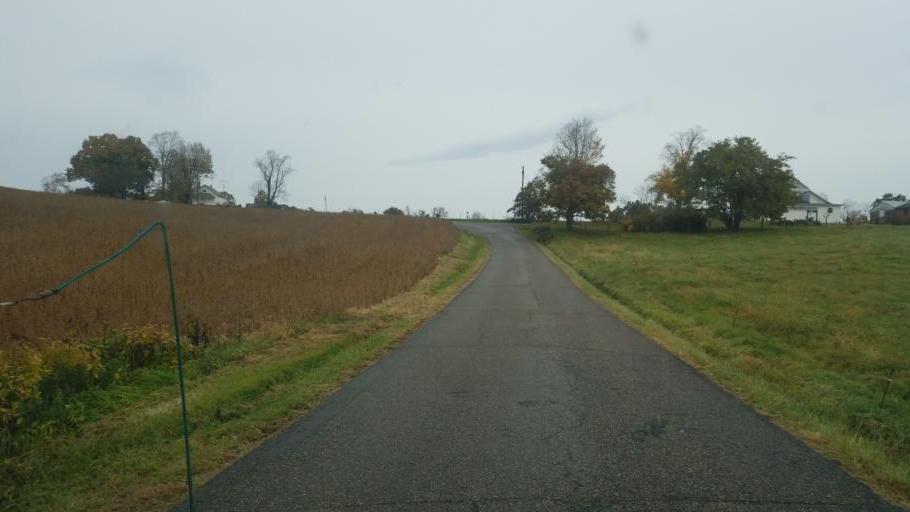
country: US
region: Ohio
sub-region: Washington County
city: Beverly
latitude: 39.5501
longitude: -81.7032
